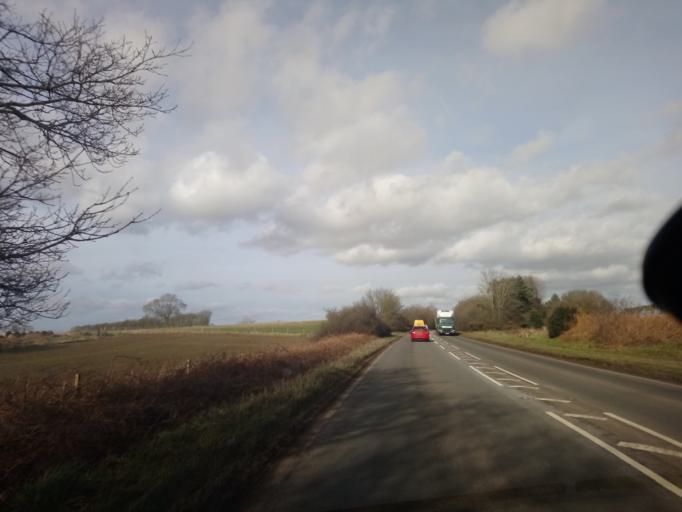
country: GB
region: England
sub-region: Telford and Wrekin
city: Eyton upon the Weald Moors
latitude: 52.7803
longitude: -2.5540
